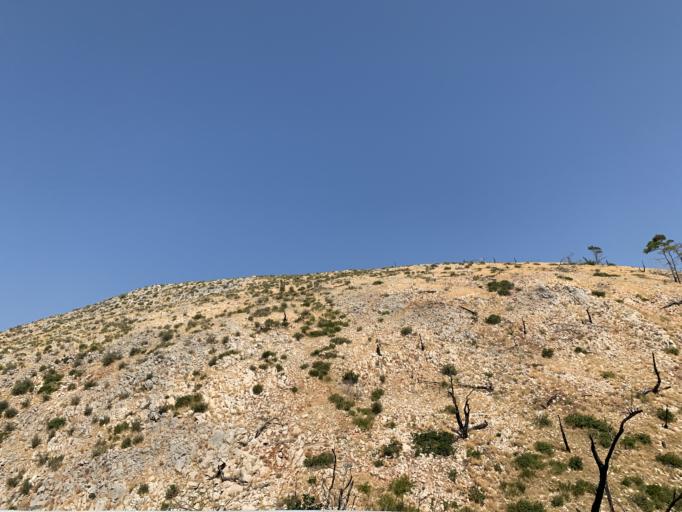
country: GR
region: North Aegean
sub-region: Chios
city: Thymiana
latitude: 38.3134
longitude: 26.0045
